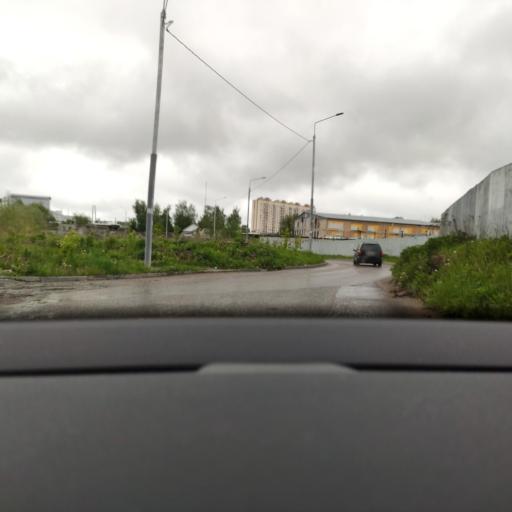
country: RU
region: Moskovskaya
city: Saltykovka
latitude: 55.7436
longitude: 37.9552
